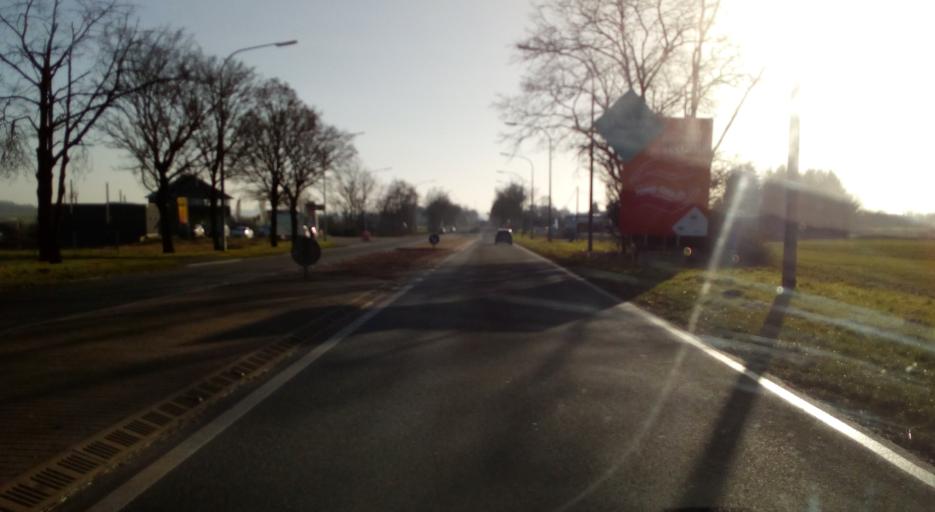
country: BE
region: Wallonia
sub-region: Province du Hainaut
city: Gerpinnes
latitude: 50.3146
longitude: 4.4789
